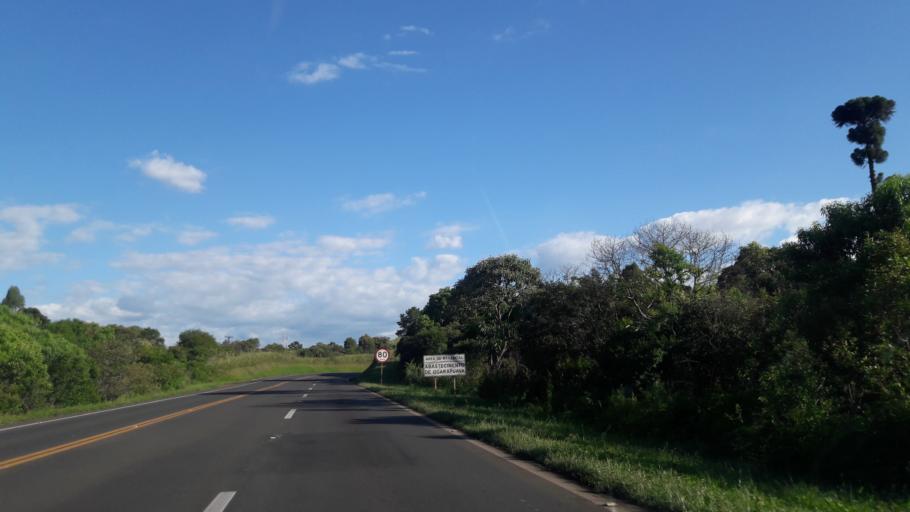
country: BR
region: Parana
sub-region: Guarapuava
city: Guarapuava
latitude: -25.3618
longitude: -51.3509
